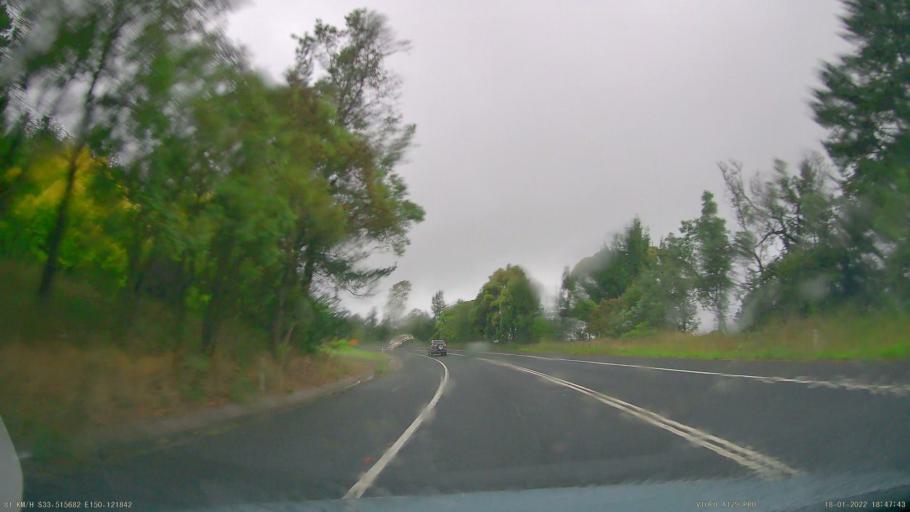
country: AU
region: New South Wales
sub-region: Lithgow
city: Bowenfels
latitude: -33.5159
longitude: 150.1219
